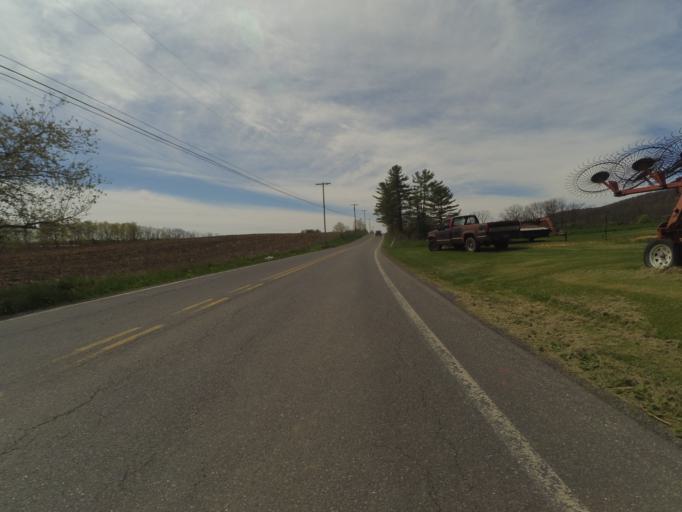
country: US
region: Pennsylvania
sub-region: Centre County
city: Stormstown
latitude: 40.7554
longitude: -78.0686
